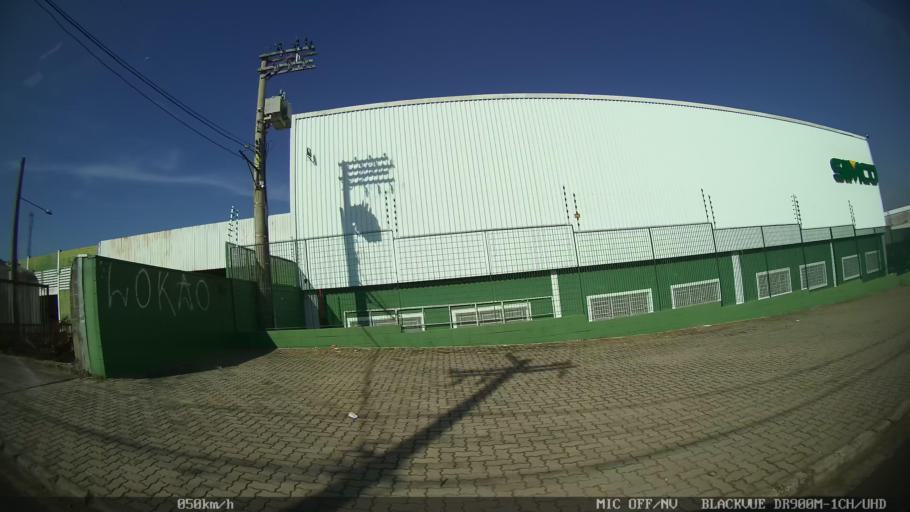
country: BR
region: Sao Paulo
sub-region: Campinas
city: Campinas
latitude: -22.9617
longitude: -47.0973
